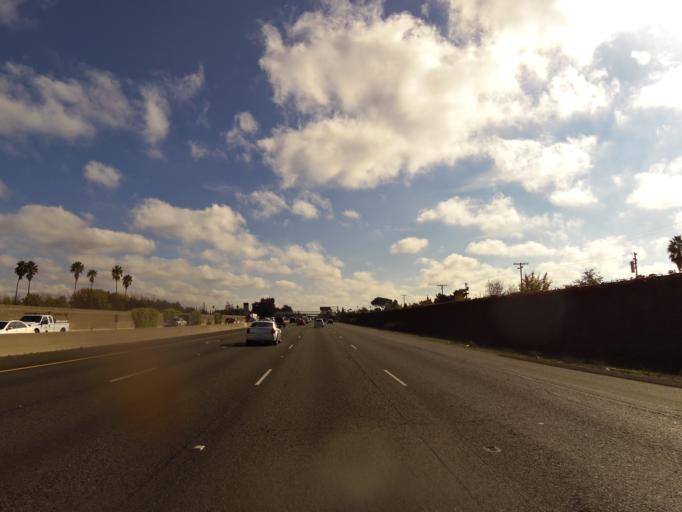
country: US
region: California
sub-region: Sacramento County
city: Parkway
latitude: 38.5054
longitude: -121.4561
